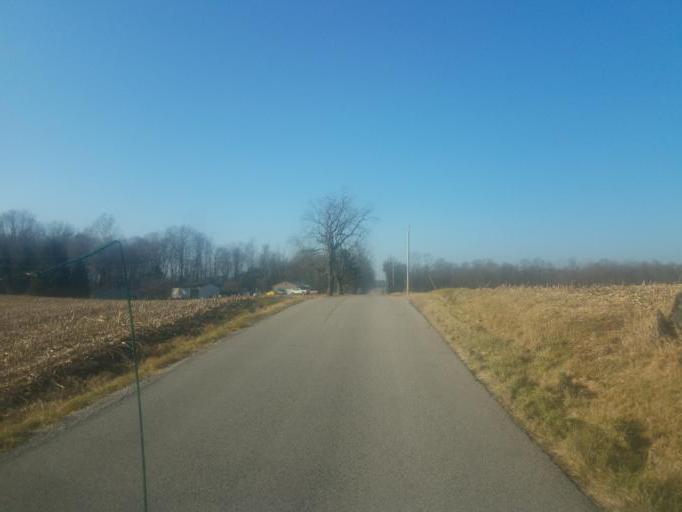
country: US
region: Ohio
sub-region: Crawford County
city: Bucyrus
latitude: 40.8287
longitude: -82.9251
